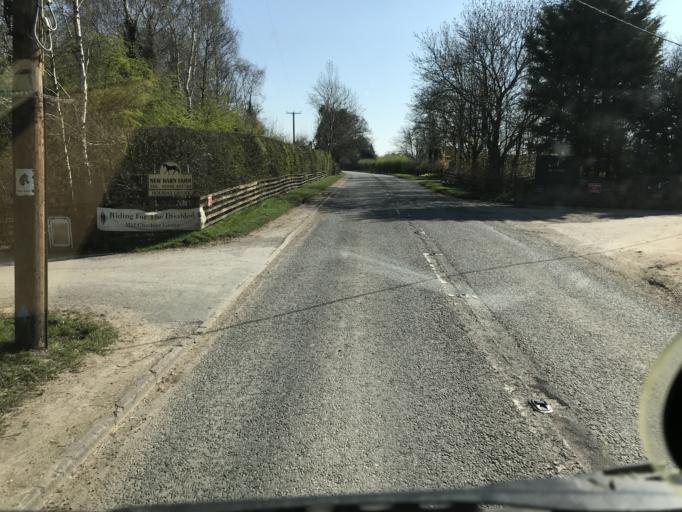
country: GB
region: England
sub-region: Cheshire East
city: Mobberley
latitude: 53.2820
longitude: -2.3157
